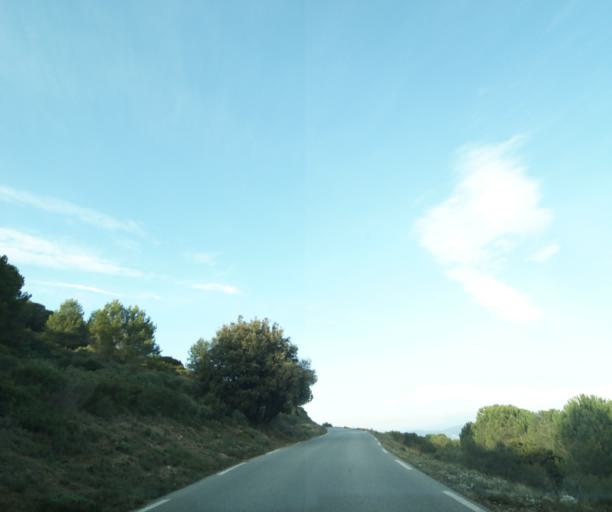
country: FR
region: Provence-Alpes-Cote d'Azur
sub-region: Departement des Bouches-du-Rhone
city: La Ciotat
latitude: 43.1821
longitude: 5.5677
